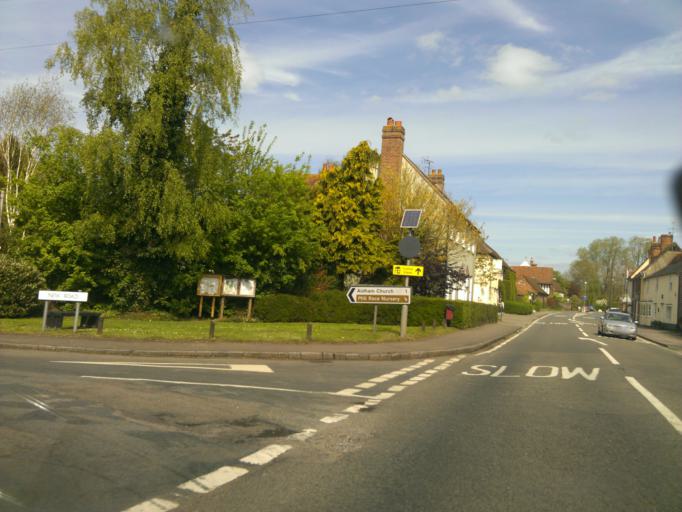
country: GB
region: England
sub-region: Essex
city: Eight Ash Green
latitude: 51.9072
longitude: 0.7910
